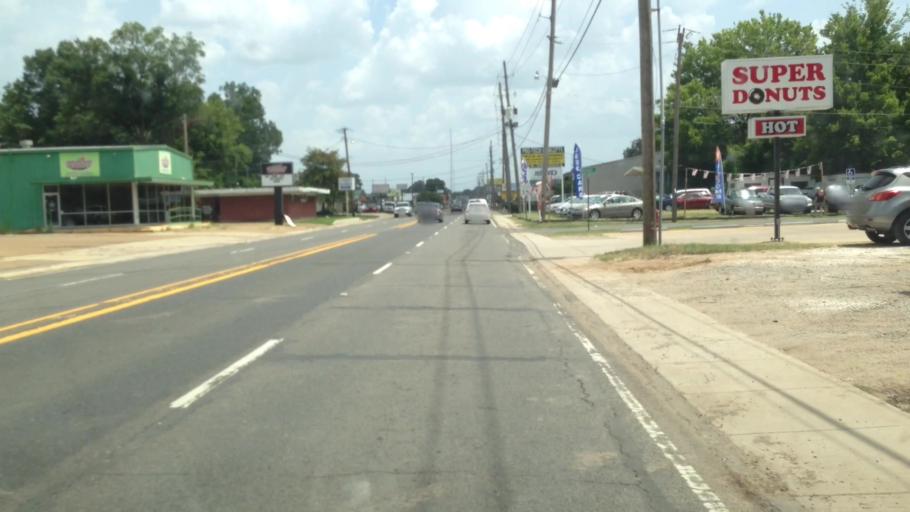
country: US
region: Louisiana
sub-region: Ouachita Parish
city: Monroe
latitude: 32.5092
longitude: -92.1331
